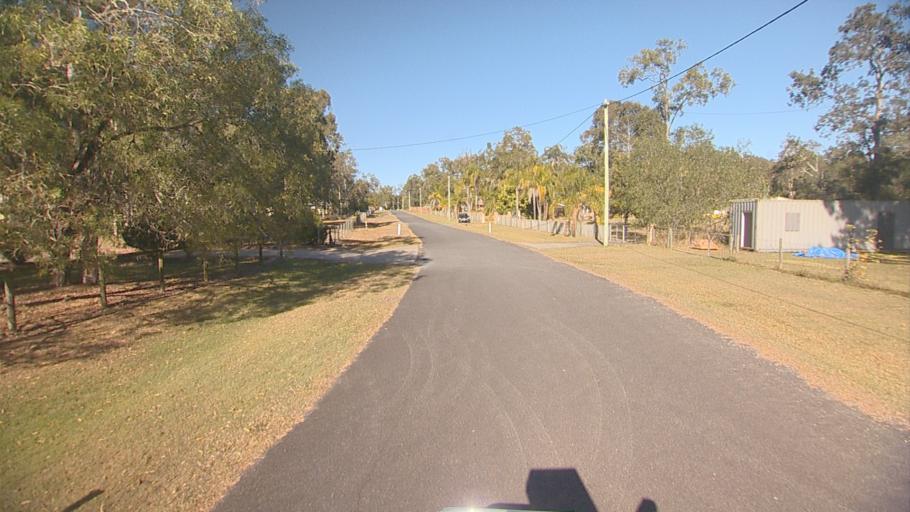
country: AU
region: Queensland
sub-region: Logan
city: Chambers Flat
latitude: -27.7486
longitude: 153.0514
